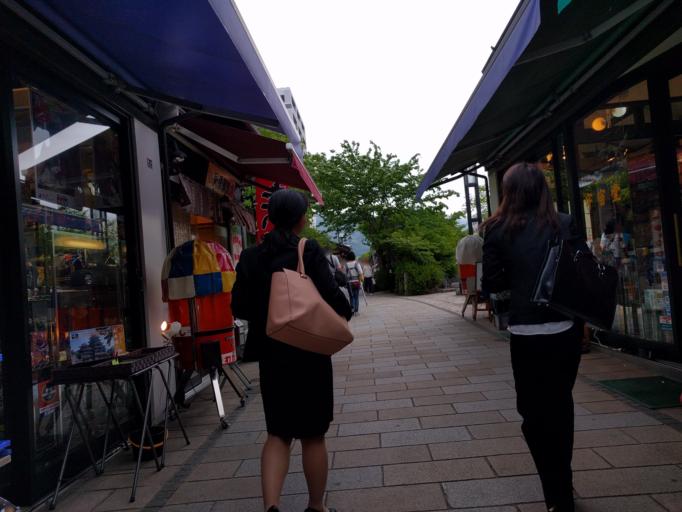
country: JP
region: Nagano
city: Matsumoto
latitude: 36.2344
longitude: 137.9701
